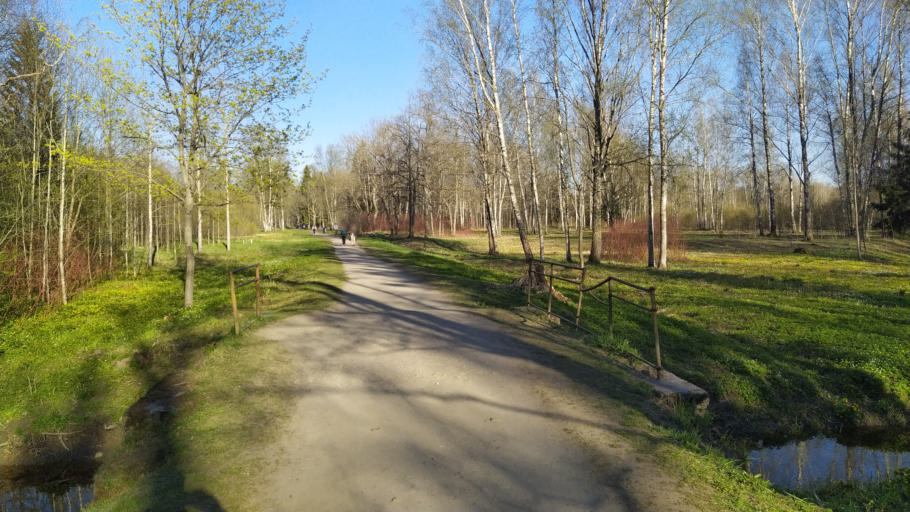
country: RU
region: St.-Petersburg
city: Aleksandrovskaya
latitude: 59.7128
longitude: 30.3580
